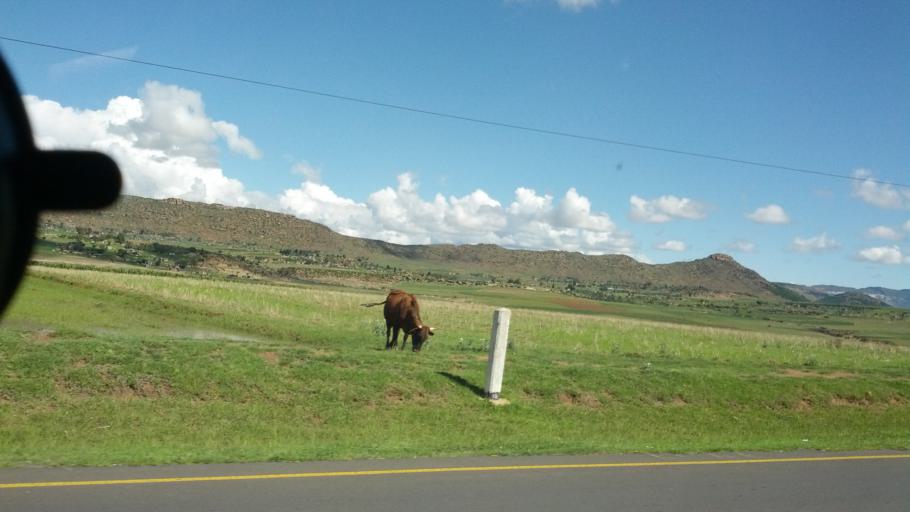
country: LS
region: Mafeteng
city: Mafeteng
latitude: -29.6504
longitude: 27.4604
